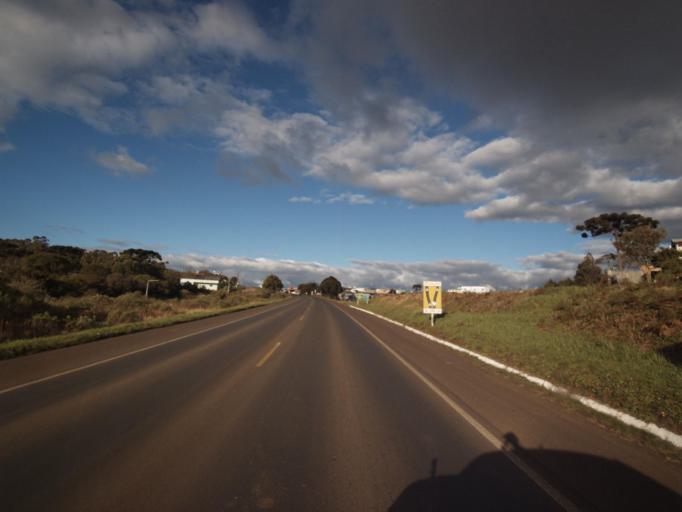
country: BR
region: Santa Catarina
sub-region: Campos Novos
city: Campos Novos
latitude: -27.3909
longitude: -51.2219
